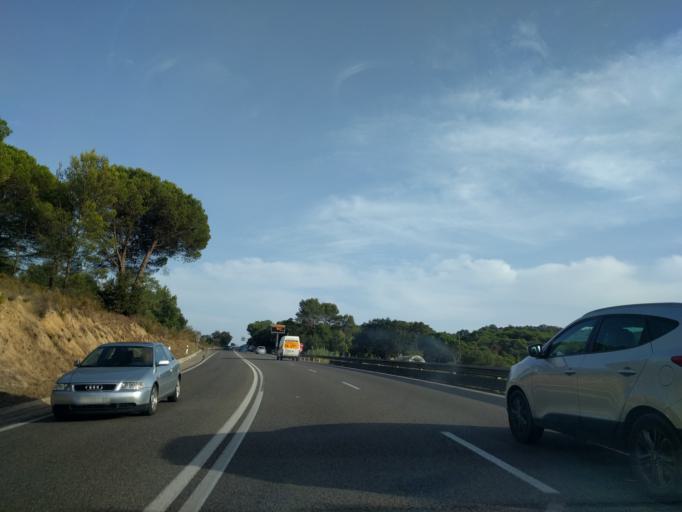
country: ES
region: Catalonia
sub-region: Provincia de Barcelona
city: Tordera
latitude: 41.6803
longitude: 2.7217
